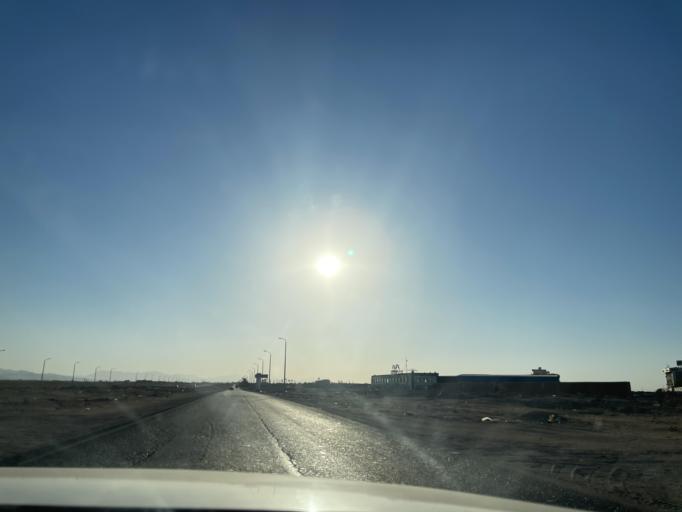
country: EG
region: Red Sea
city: Hurghada
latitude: 27.2171
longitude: 33.8015
